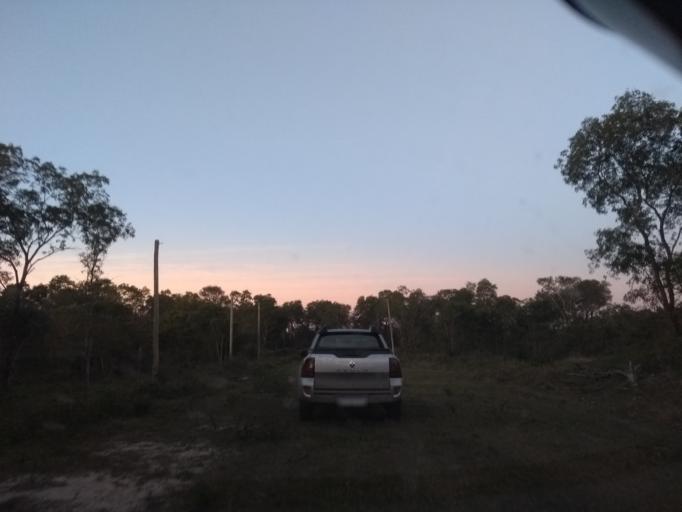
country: AR
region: Corrientes
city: Paso de la Patria
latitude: -27.3515
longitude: -58.6278
